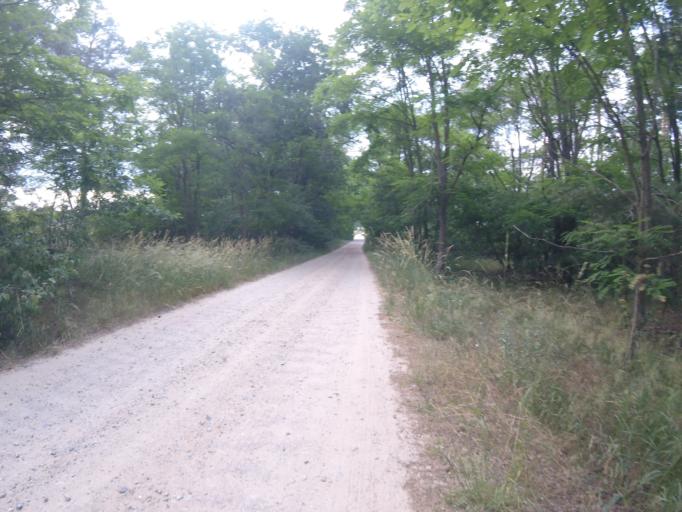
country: DE
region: Brandenburg
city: Bestensee
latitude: 52.2531
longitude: 13.6245
